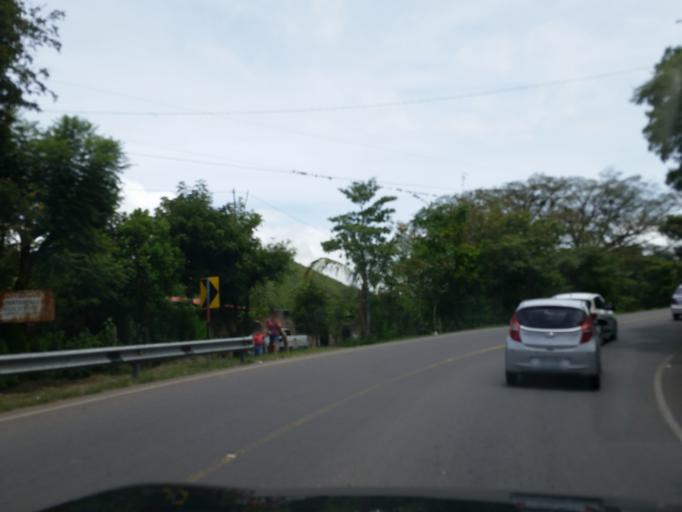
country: NI
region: Matagalpa
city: Matagalpa
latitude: 12.9436
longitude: -85.9258
